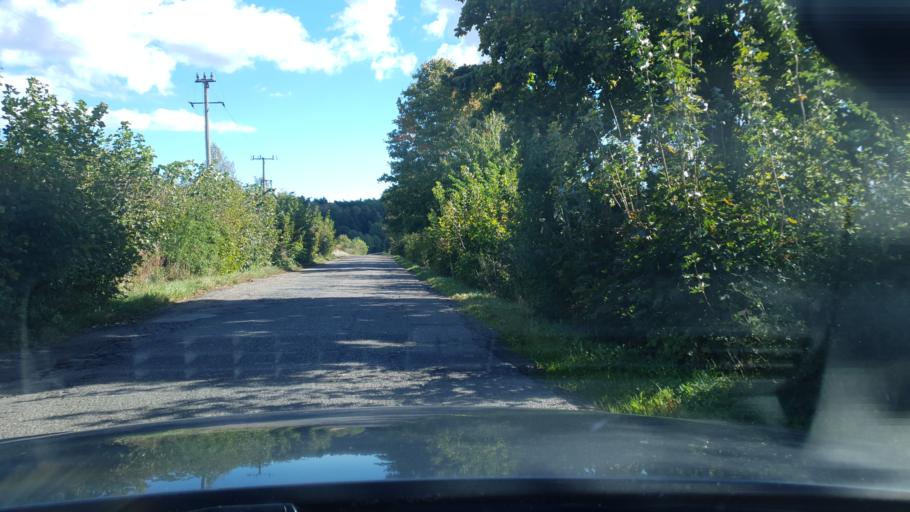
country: PL
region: Pomeranian Voivodeship
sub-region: Powiat pucki
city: Zelistrzewo
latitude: 54.6903
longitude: 18.4198
